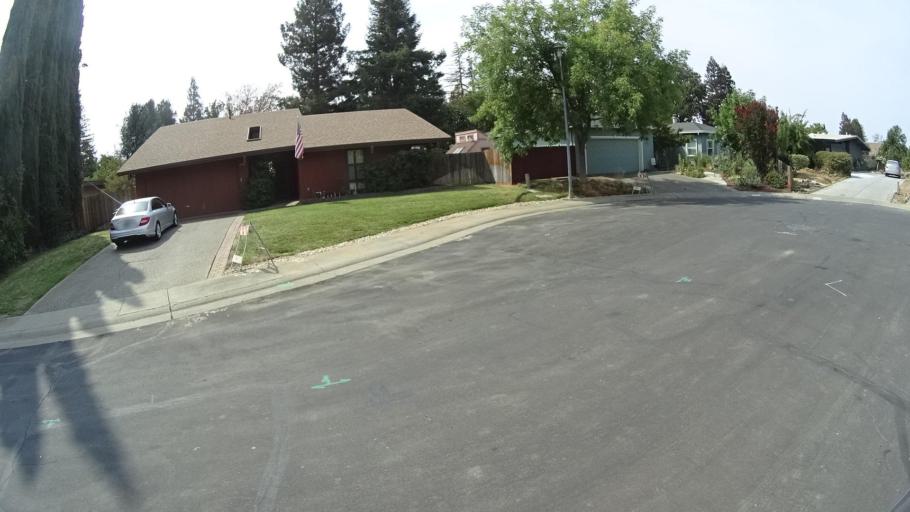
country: US
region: California
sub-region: Sacramento County
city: Elk Grove
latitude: 38.4152
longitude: -121.3801
